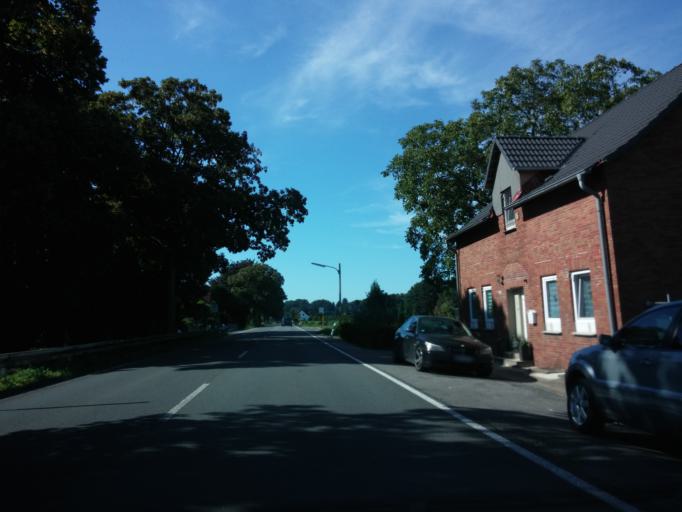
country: DE
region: North Rhine-Westphalia
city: Dorsten
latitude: 51.6297
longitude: 7.0052
